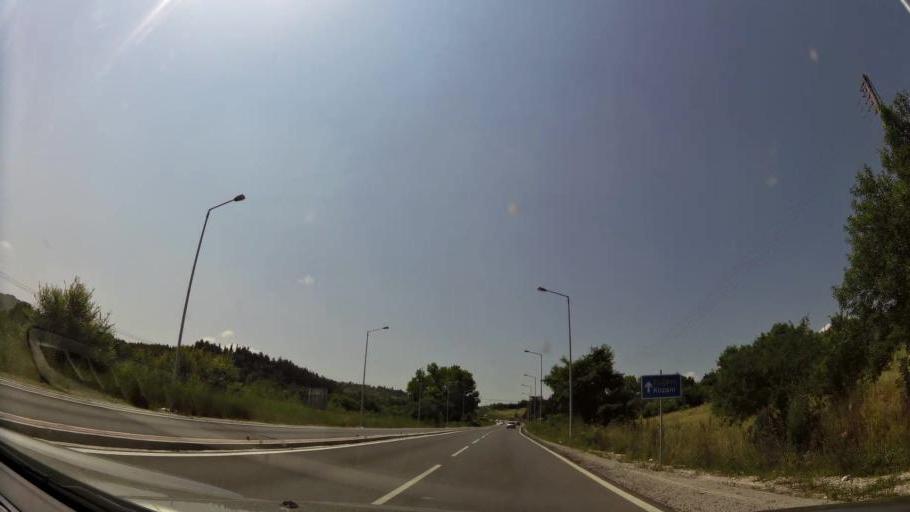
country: GR
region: West Macedonia
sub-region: Nomos Kozanis
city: Koila
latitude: 40.3245
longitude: 21.7881
